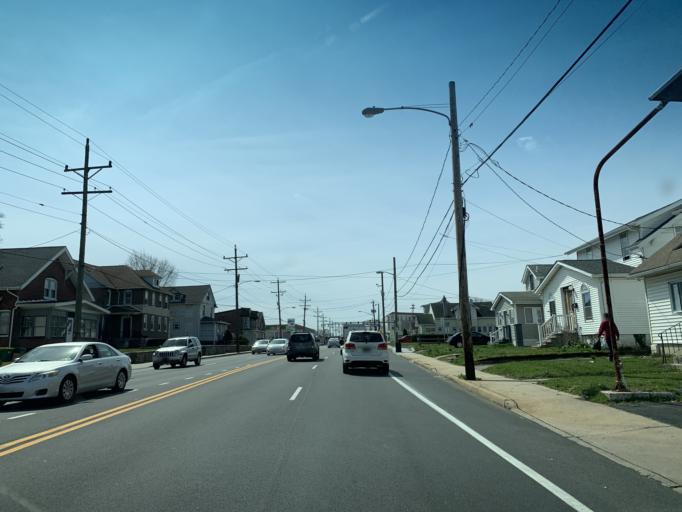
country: US
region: Delaware
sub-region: New Castle County
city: Elsmere
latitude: 39.7282
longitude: -75.5866
